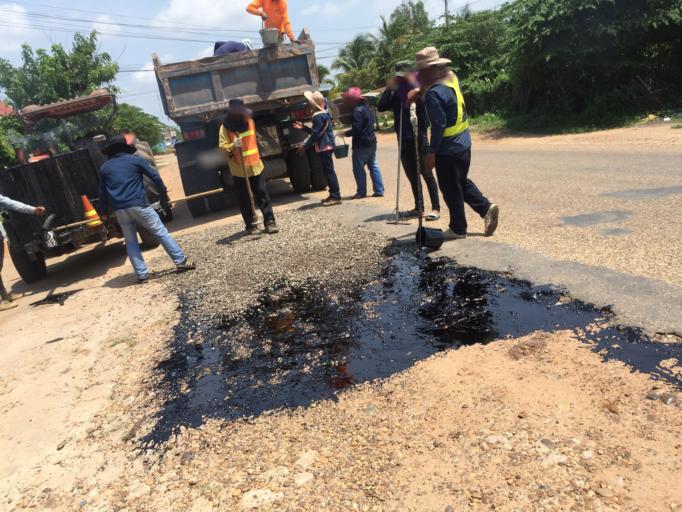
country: LA
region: Savannahkhet
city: Savannakhet
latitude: 16.5394
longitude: 104.7725
